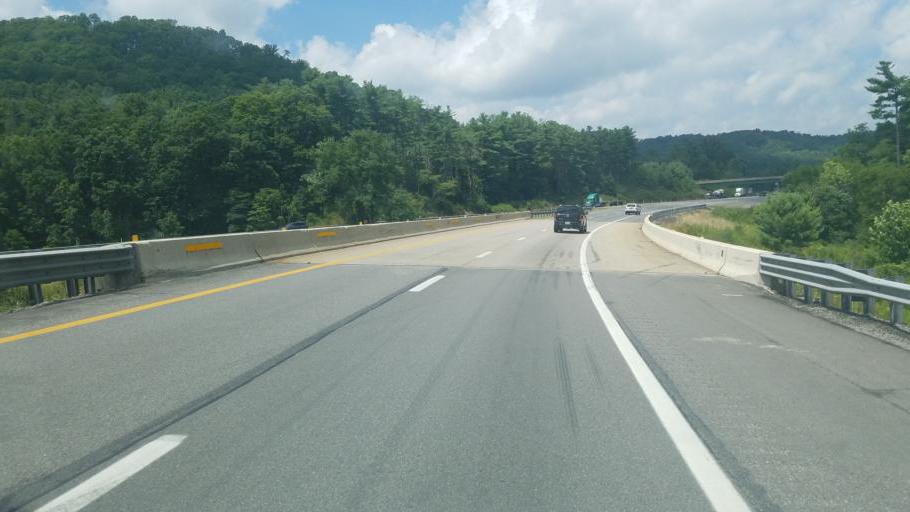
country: US
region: West Virginia
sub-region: Raleigh County
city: Beaver
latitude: 37.7100
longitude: -81.1507
